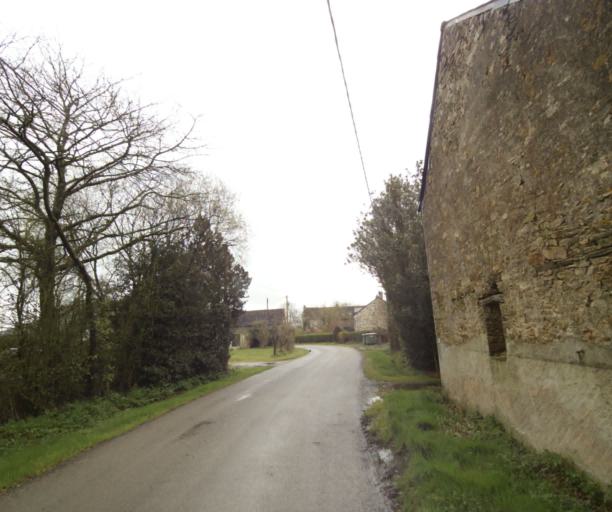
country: FR
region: Pays de la Loire
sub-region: Departement de la Loire-Atlantique
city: Bouvron
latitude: 47.4395
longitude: -1.8825
